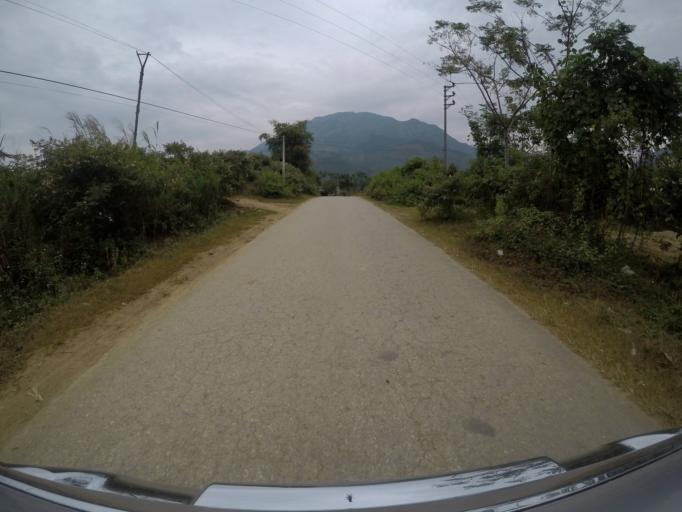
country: VN
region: Yen Bai
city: Son Thinh
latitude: 21.6579
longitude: 104.5012
